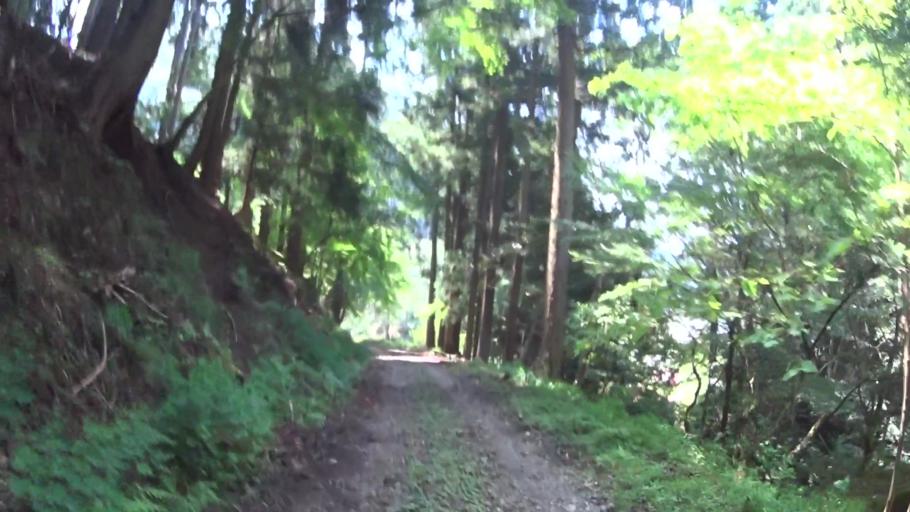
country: JP
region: Kyoto
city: Maizuru
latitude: 35.3260
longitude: 135.4608
